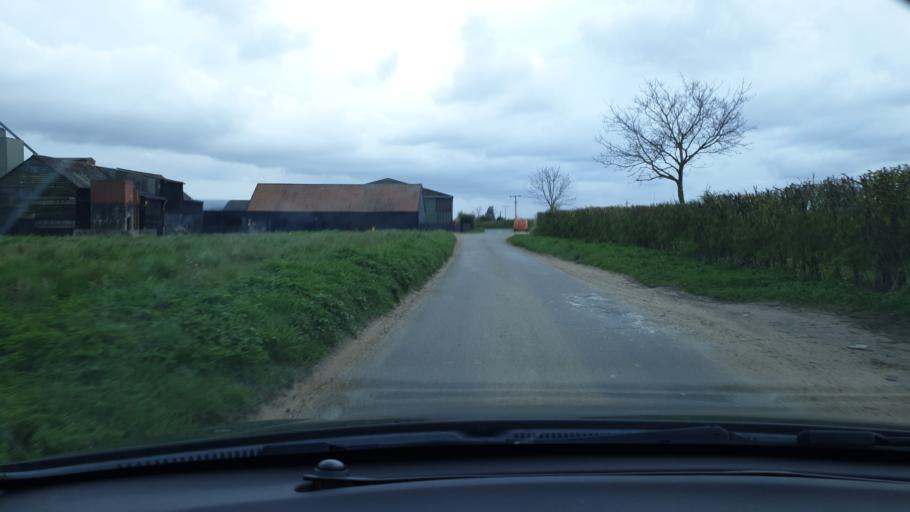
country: GB
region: England
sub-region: Suffolk
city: Shotley Gate
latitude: 51.9256
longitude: 1.1779
